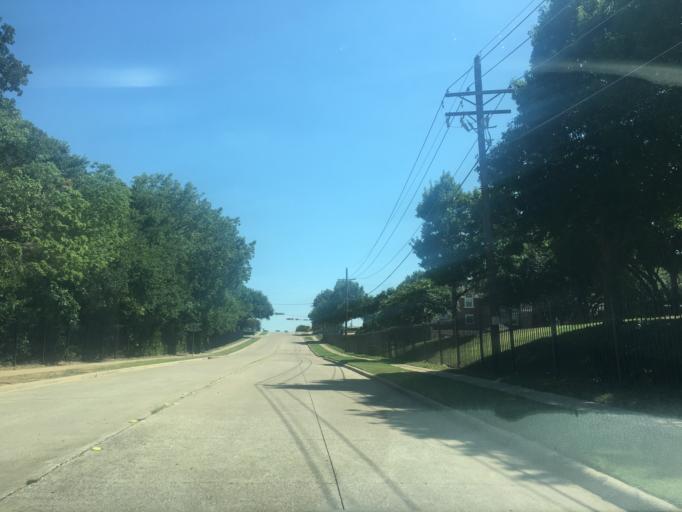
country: US
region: Texas
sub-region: Denton County
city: Lewisville
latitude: 33.0055
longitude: -96.9897
